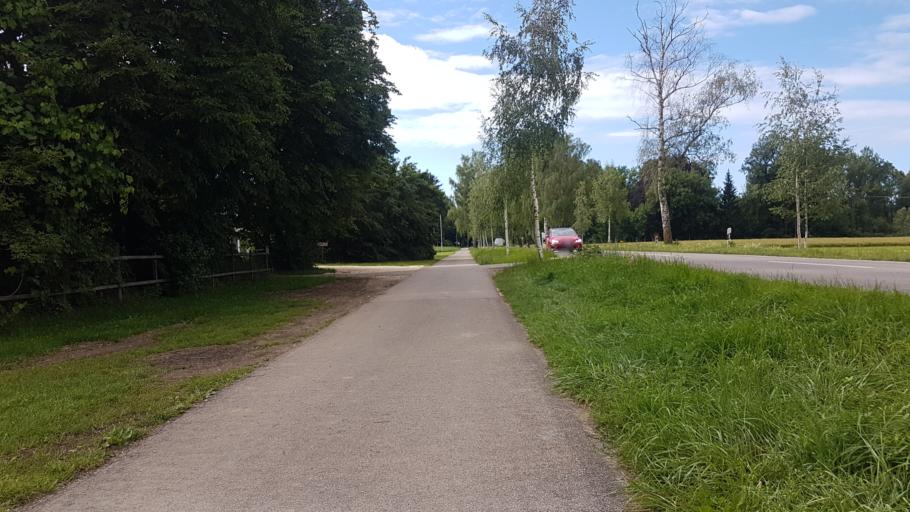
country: DE
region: Bavaria
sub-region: Swabia
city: Guenzburg
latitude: 48.4711
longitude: 10.2642
